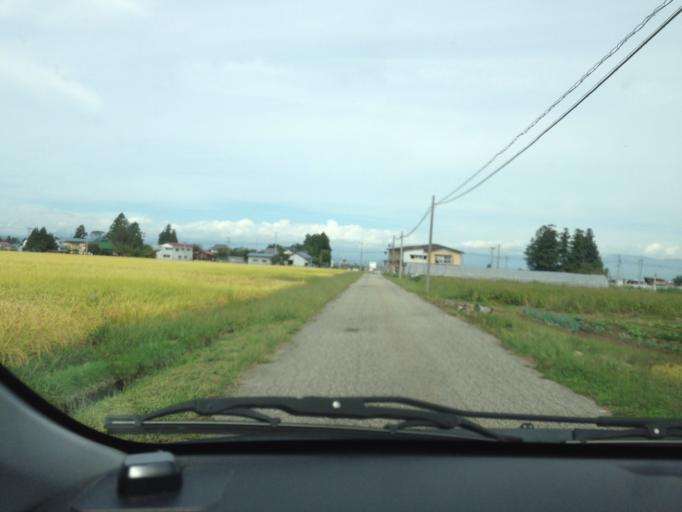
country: JP
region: Fukushima
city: Kitakata
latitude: 37.5126
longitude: 139.8649
